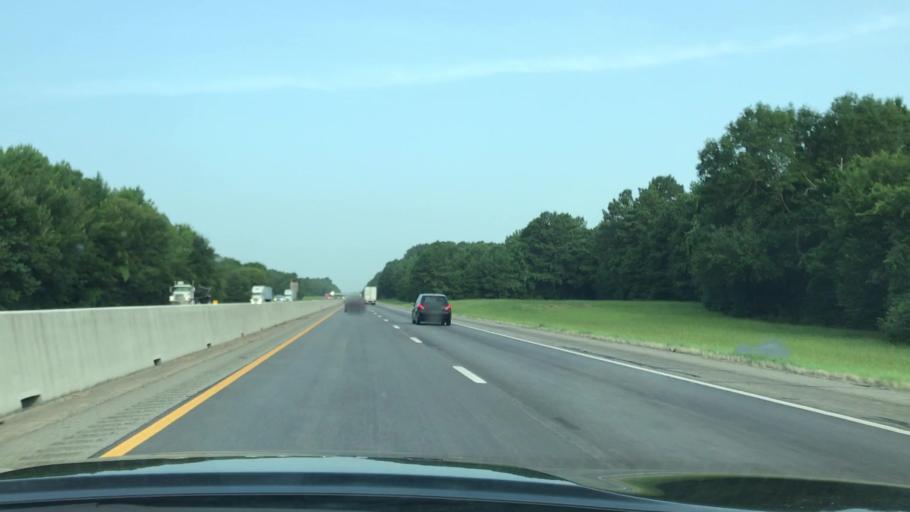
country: US
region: Texas
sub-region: Gregg County
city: Kilgore
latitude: 32.4327
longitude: -94.8893
